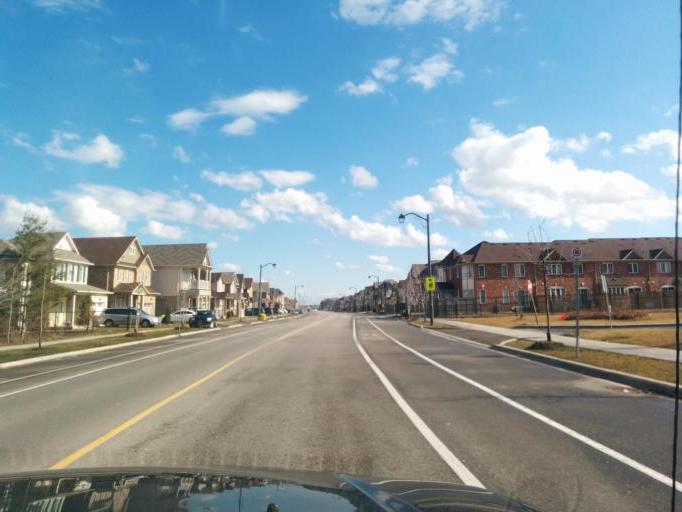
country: CA
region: Ontario
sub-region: Halton
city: Milton
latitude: 43.4965
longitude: -79.8607
